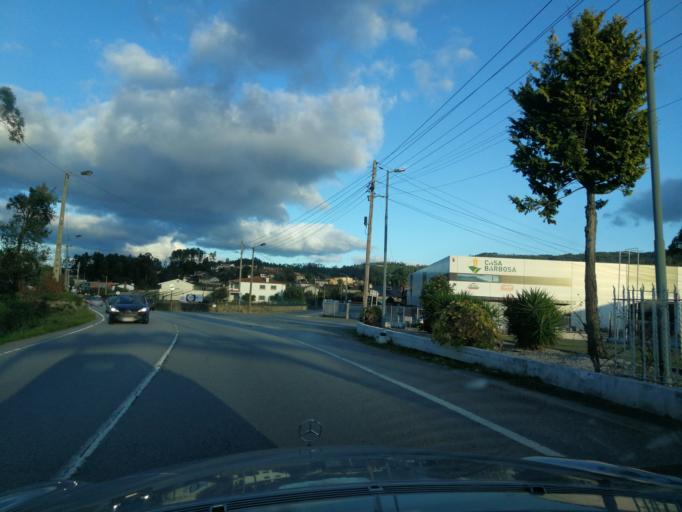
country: PT
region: Braga
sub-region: Barcelos
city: Galegos
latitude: 41.5209
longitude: -8.5705
